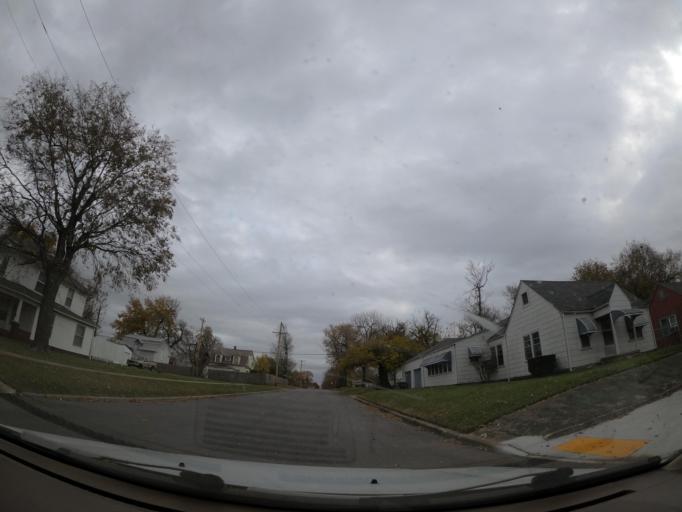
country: US
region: Oklahoma
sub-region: Tulsa County
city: Tulsa
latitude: 36.1638
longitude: -95.9658
